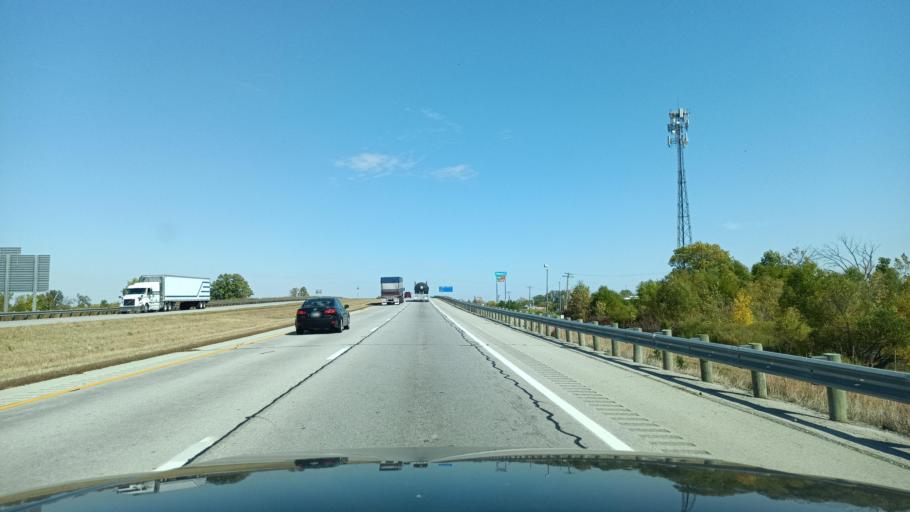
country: US
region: Ohio
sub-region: Henry County
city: Napoleon
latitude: 41.4035
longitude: -84.1383
